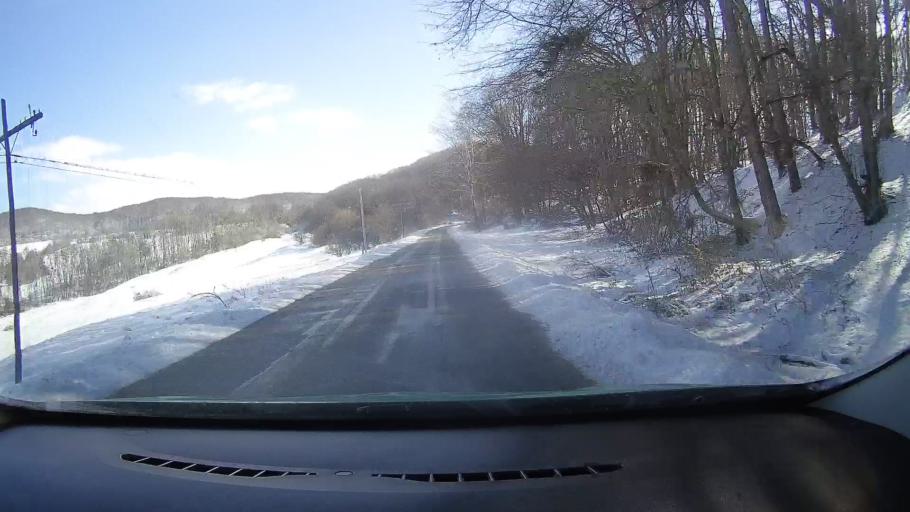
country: RO
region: Sibiu
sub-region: Comuna Mosna
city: Mosna
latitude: 46.0176
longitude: 24.4200
